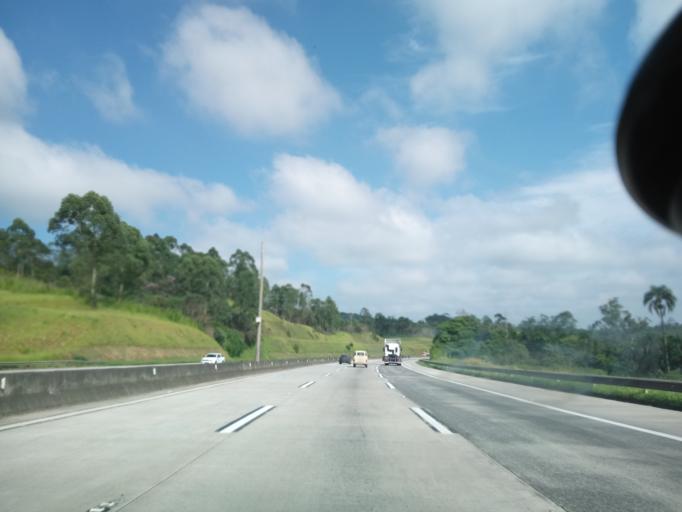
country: BR
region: Sao Paulo
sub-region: Itapecerica Da Serra
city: Itapecerica da Serra
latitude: -23.7475
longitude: -46.8093
